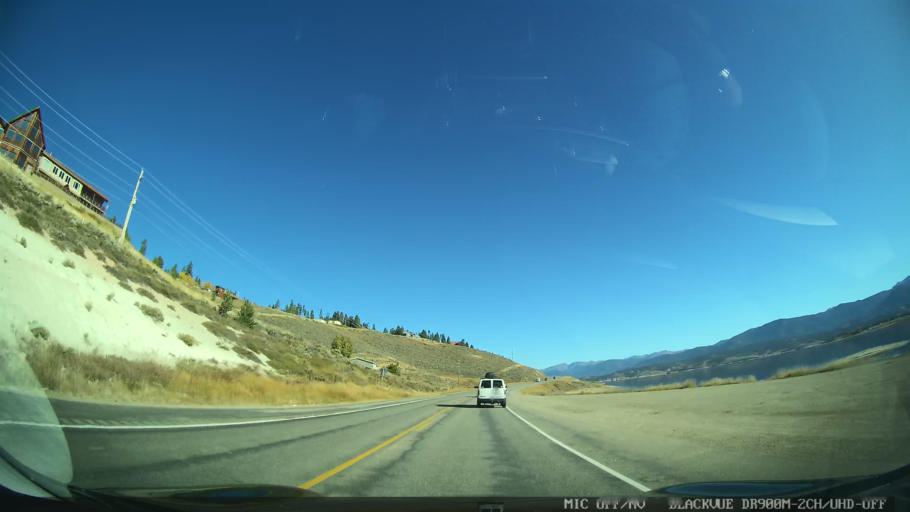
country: US
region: Colorado
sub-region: Grand County
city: Granby
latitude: 40.1461
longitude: -105.8905
